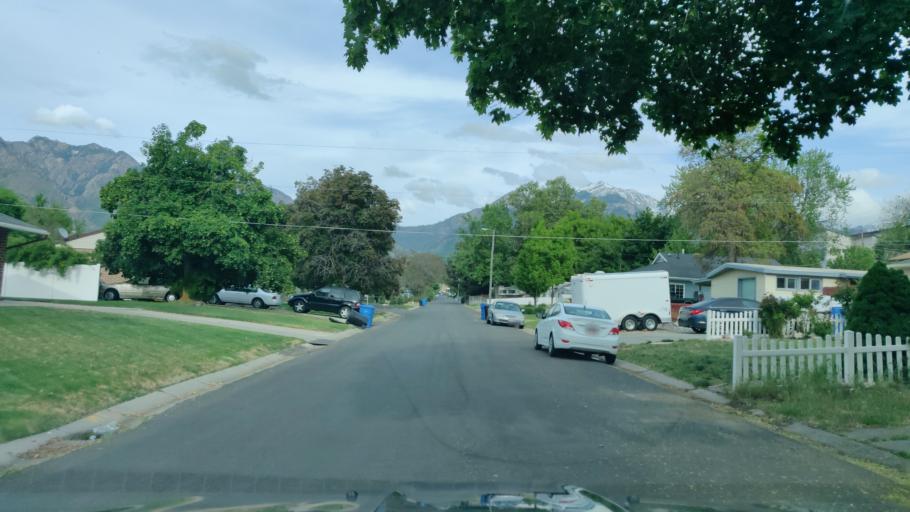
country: US
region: Utah
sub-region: Salt Lake County
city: Little Cottonwood Creek Valley
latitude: 40.6260
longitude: -111.8440
